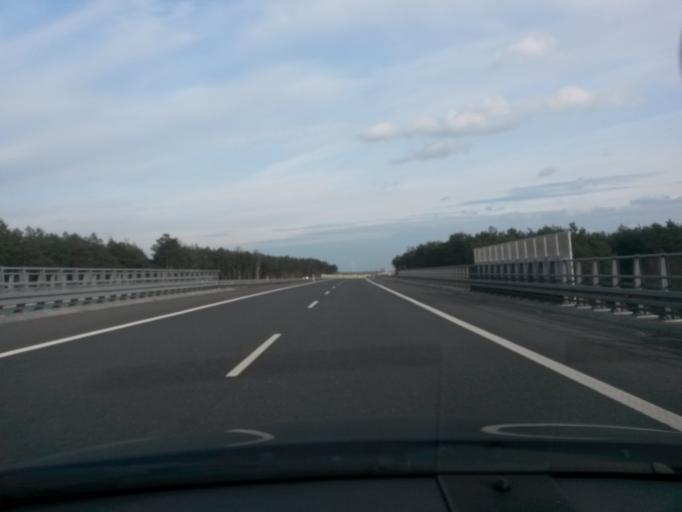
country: PL
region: Lodz Voivodeship
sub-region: Powiat leczycki
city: Swinice Warckie
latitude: 52.0262
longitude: 18.9146
